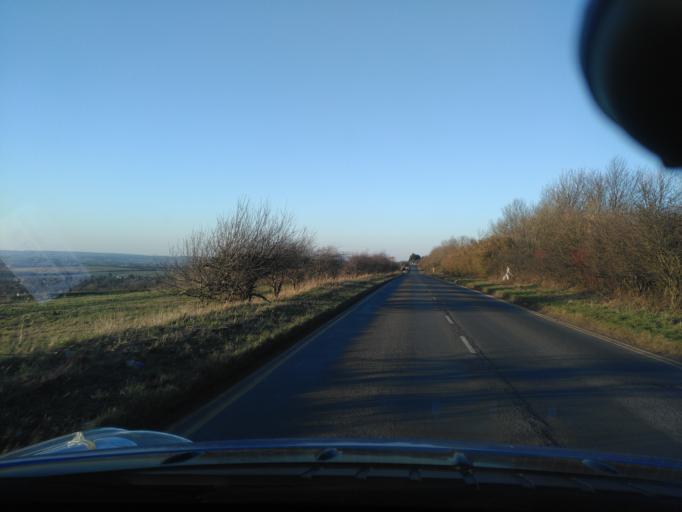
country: GB
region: England
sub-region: Central Bedfordshire
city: Dunstable
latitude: 51.8704
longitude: -0.5369
